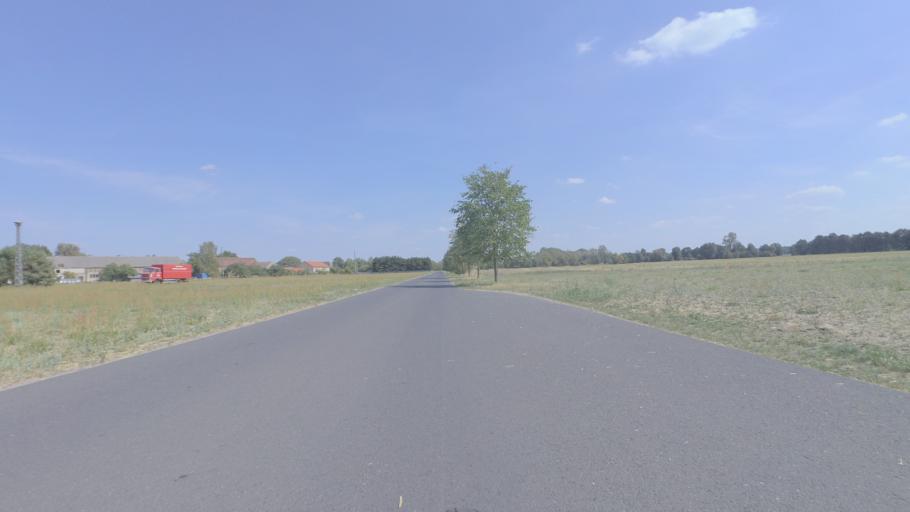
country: DE
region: Brandenburg
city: Trebbin
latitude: 52.1842
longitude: 13.2840
